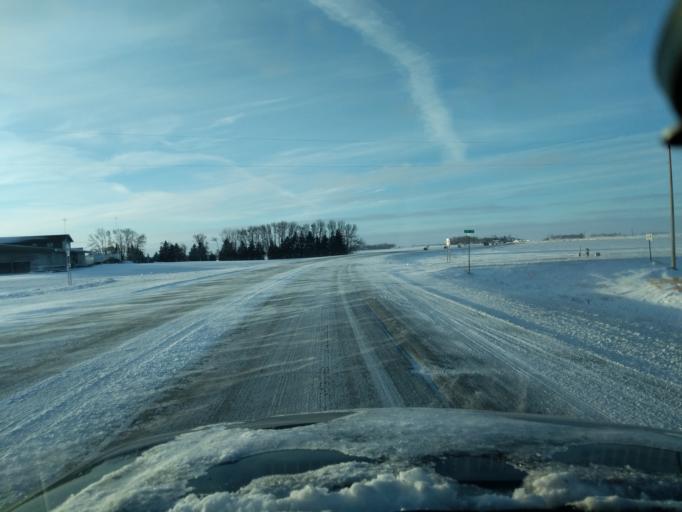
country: US
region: Minnesota
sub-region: Renville County
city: Bird Island
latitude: 44.7679
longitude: -94.9354
